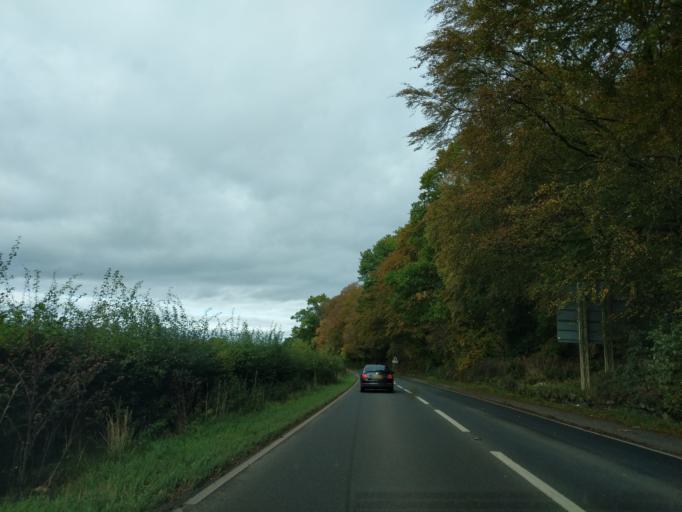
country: GB
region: Scotland
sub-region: Dumfries and Galloway
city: Thornhill
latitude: 55.2517
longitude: -3.7728
